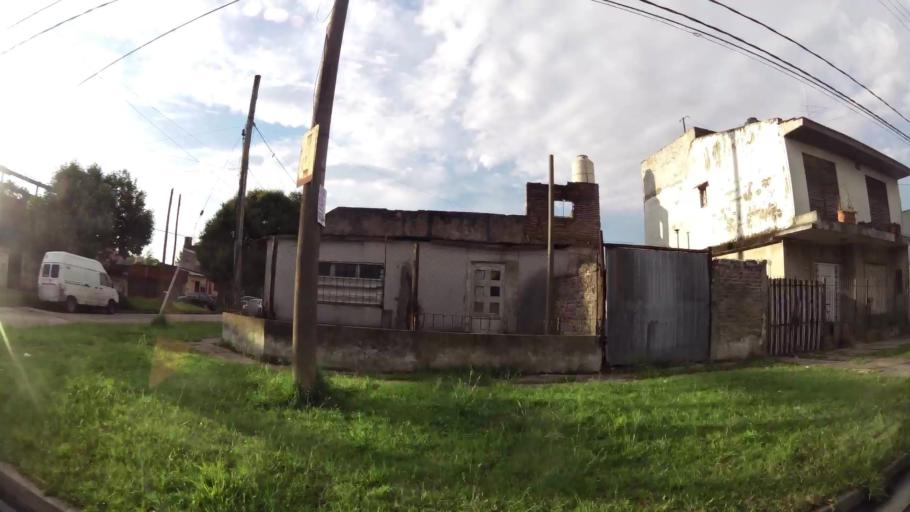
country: AR
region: Buenos Aires
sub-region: Partido de Lomas de Zamora
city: Lomas de Zamora
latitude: -34.7567
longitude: -58.3555
